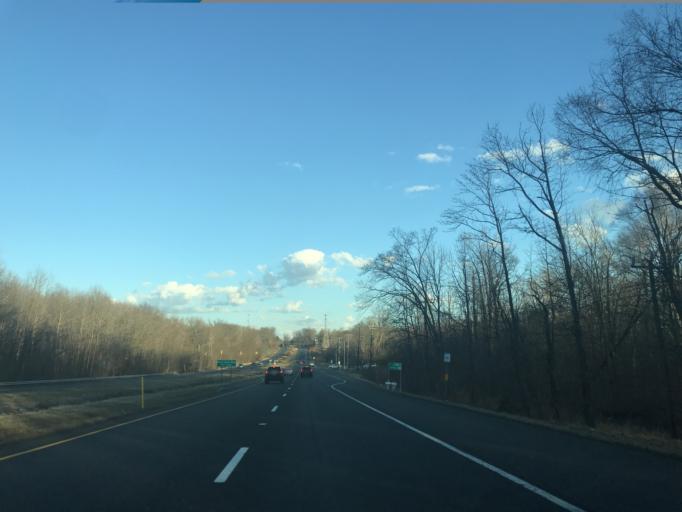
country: US
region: Maryland
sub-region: Prince George's County
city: Kettering
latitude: 38.8766
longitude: -76.8056
